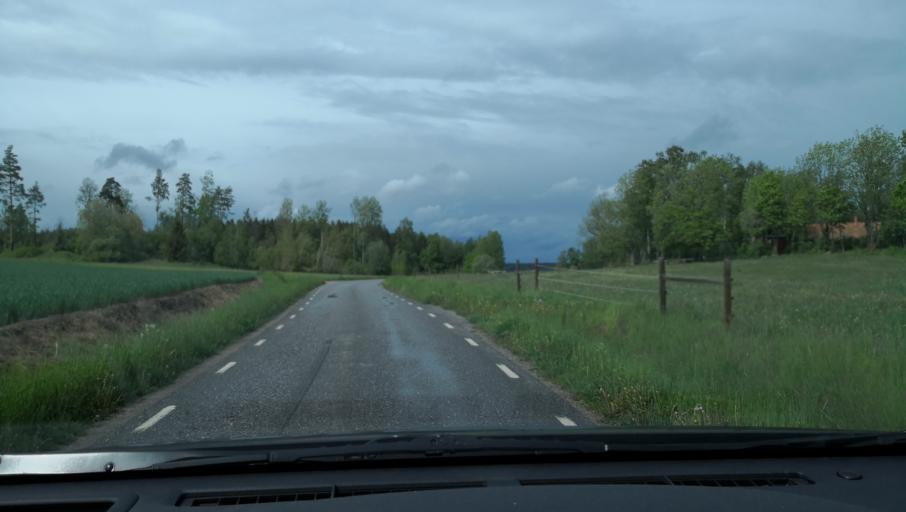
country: SE
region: Uppsala
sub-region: Enkopings Kommun
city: Orsundsbro
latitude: 59.7086
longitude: 17.4225
